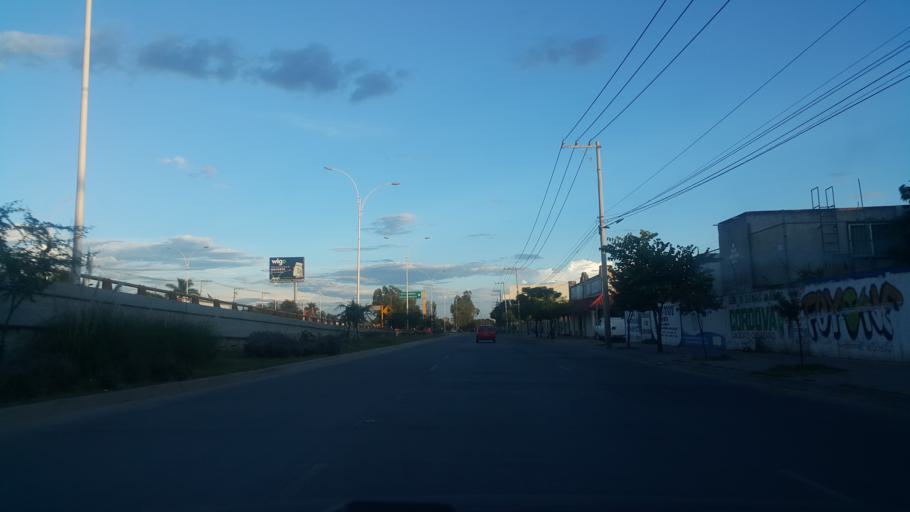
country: MX
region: Guanajuato
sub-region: Leon
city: Medina
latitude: 21.1616
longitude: -101.6472
